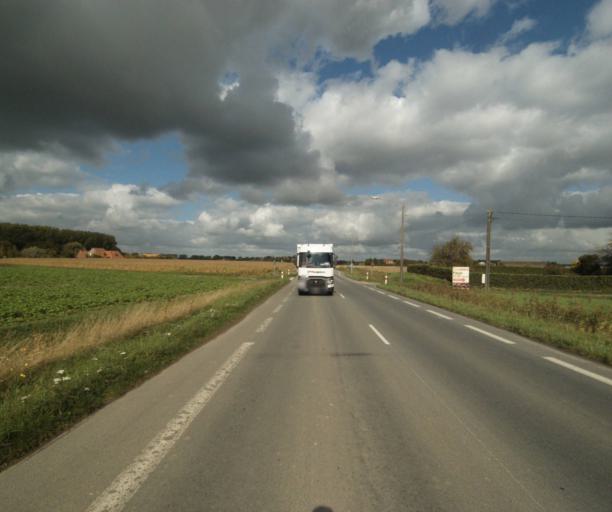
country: FR
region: Nord-Pas-de-Calais
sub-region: Departement du Nord
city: Frelinghien
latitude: 50.7157
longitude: 2.9397
